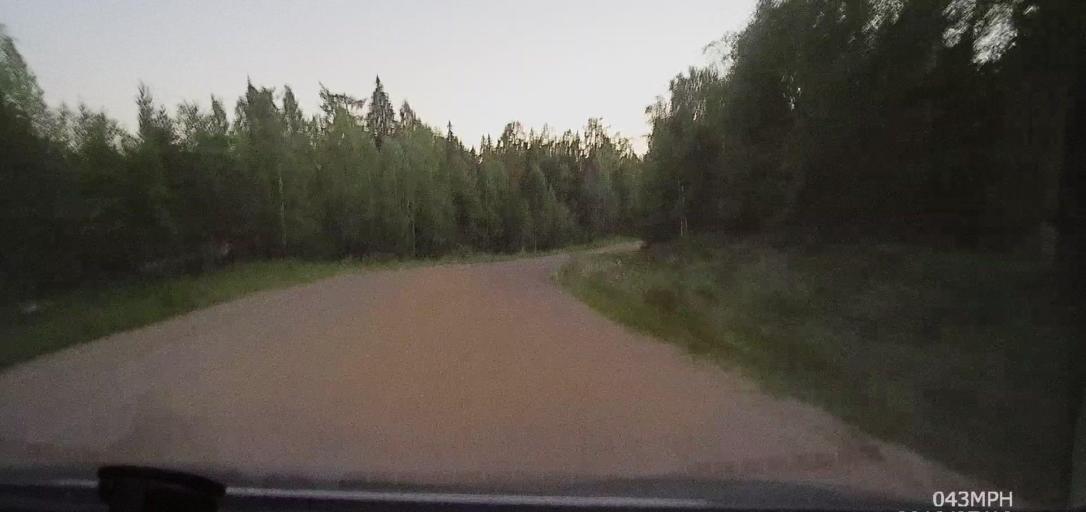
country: RU
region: Arkhangelskaya
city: Pinega
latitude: 64.4226
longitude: 43.1421
